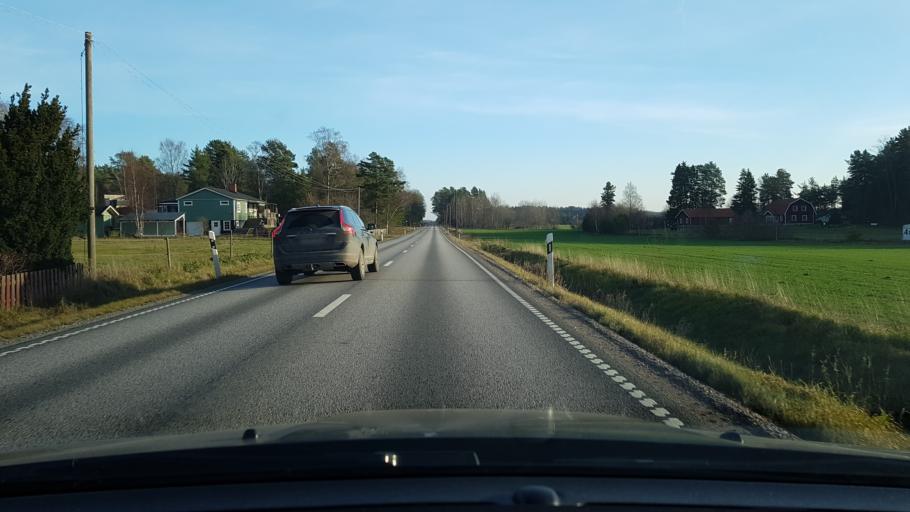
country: SE
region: Stockholm
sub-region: Norrtalje Kommun
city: Nykvarn
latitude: 59.7461
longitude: 18.1023
